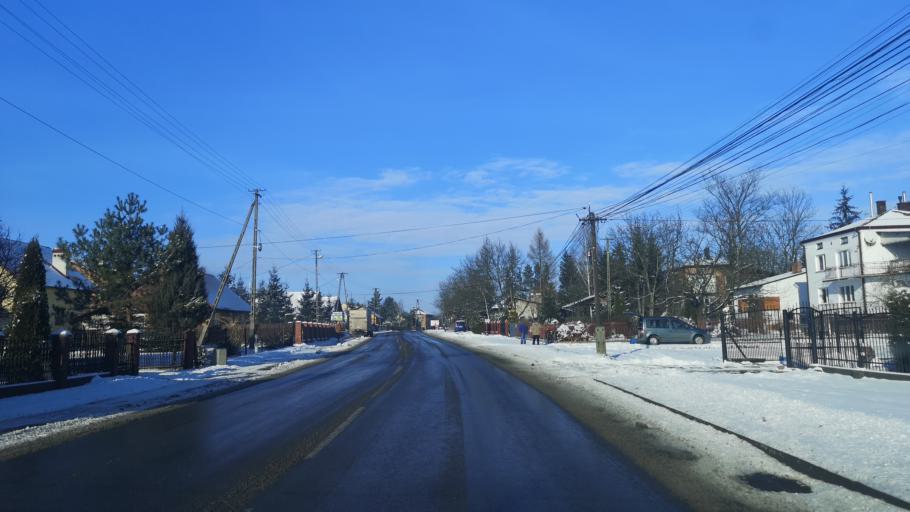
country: PL
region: Subcarpathian Voivodeship
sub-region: Powiat przeworski
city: Gorliczyna
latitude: 50.0897
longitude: 22.4916
